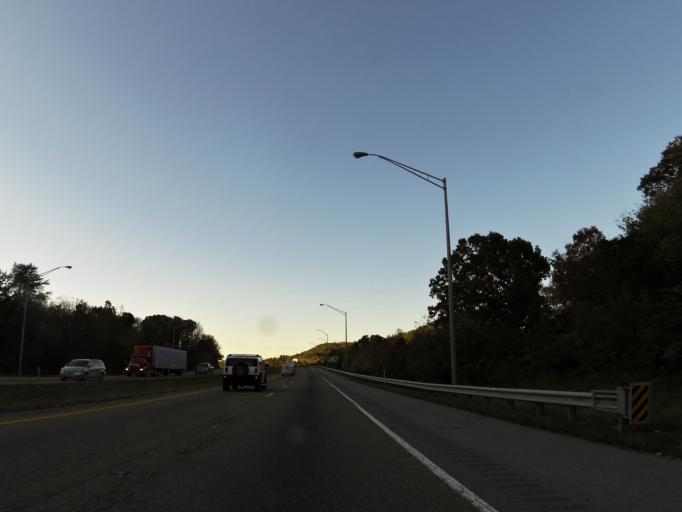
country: US
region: Tennessee
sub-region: Anderson County
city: Rocky Top
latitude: 36.2235
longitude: -84.1493
